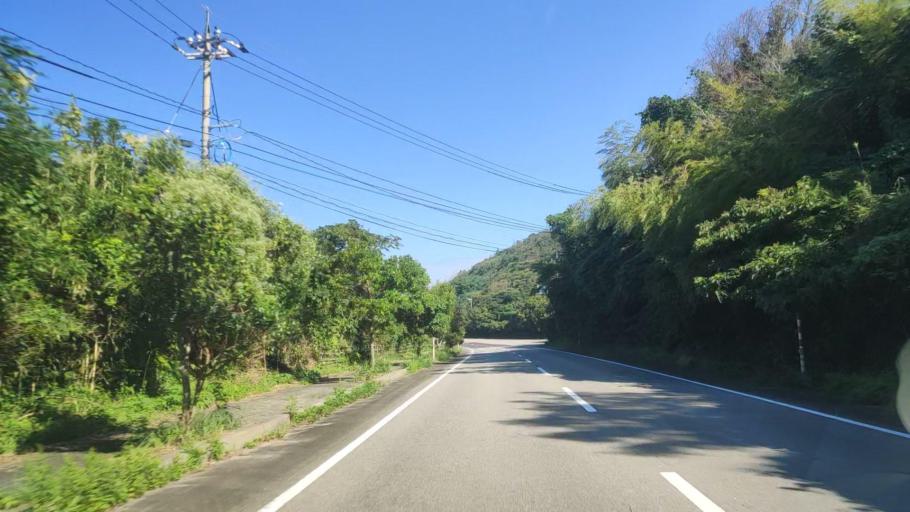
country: JP
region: Ishikawa
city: Hakui
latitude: 37.1089
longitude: 136.7285
